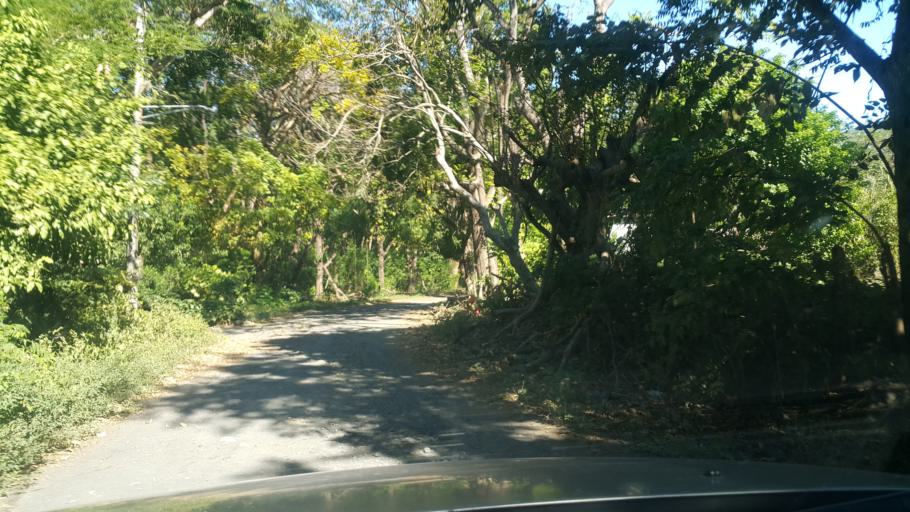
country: NI
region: Rivas
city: Altagracia
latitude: 11.4897
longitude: -85.6070
